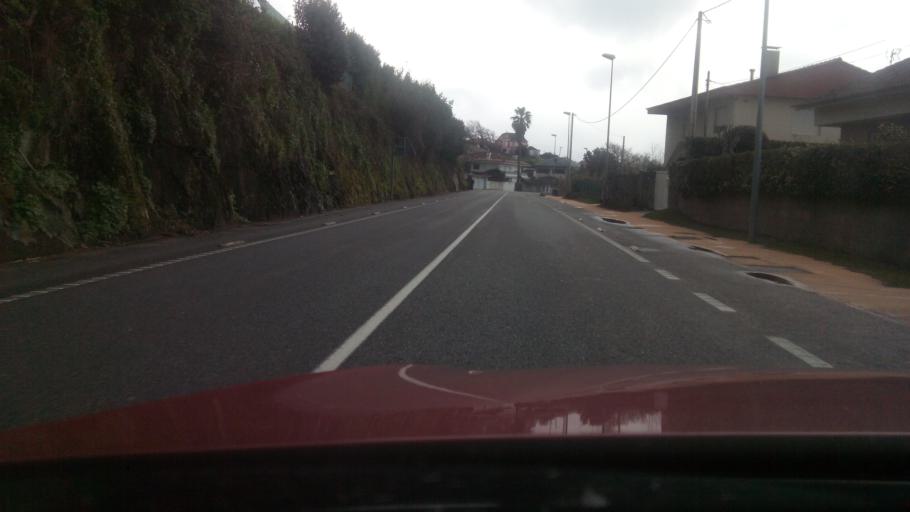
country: ES
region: Galicia
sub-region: Provincia de Pontevedra
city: Nigran
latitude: 42.1589
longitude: -8.8164
